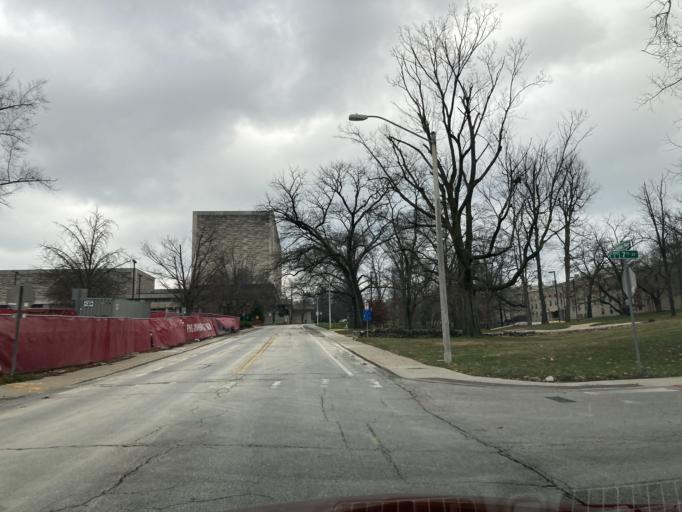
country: US
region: Indiana
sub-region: Monroe County
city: Bloomington
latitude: 39.1688
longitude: -86.5161
